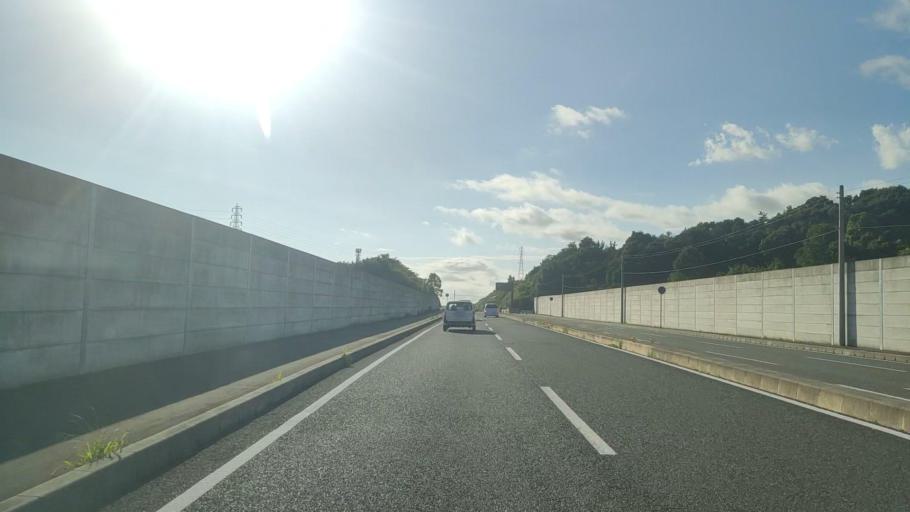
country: JP
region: Wakayama
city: Tanabe
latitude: 33.7473
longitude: 135.3650
